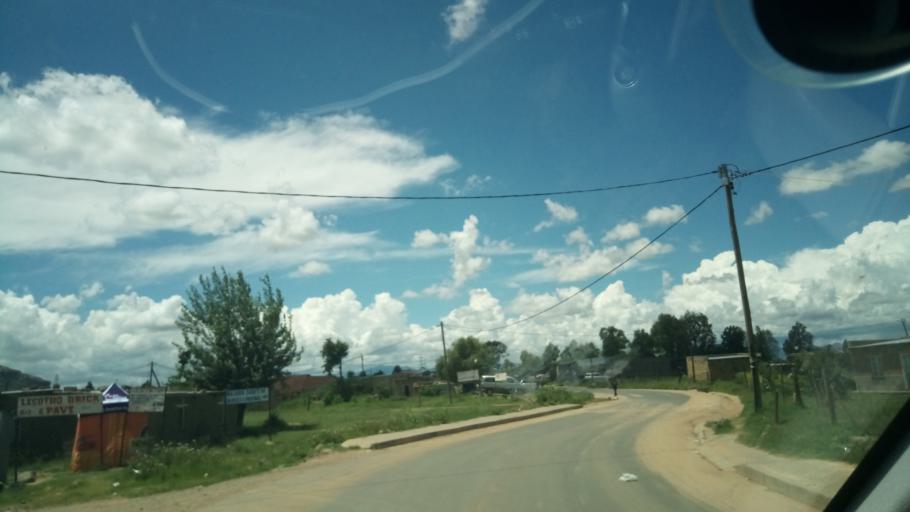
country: LS
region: Maseru
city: Maseru
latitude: -29.3661
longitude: 27.5412
